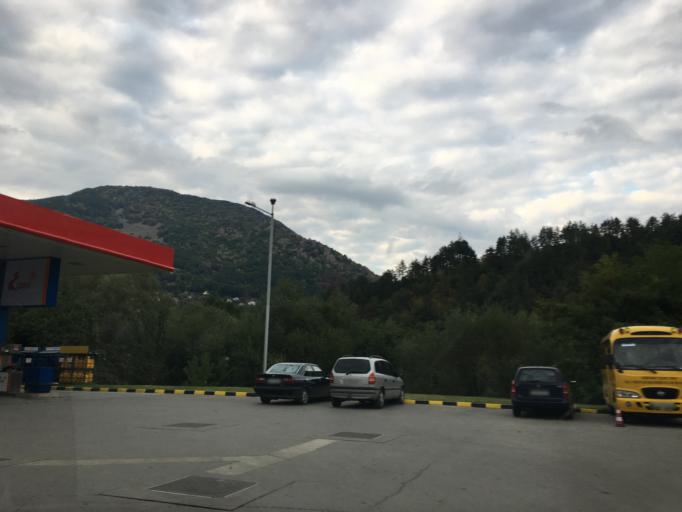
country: BG
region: Sofiya
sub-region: Obshtina Svoge
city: Svoge
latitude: 42.9613
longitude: 23.3481
